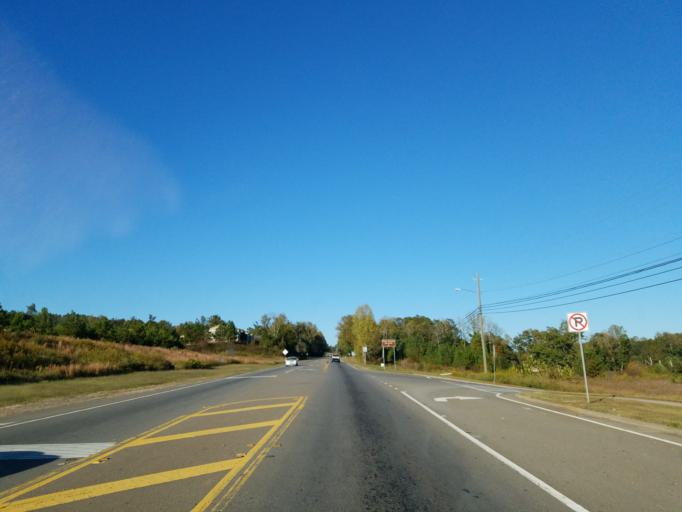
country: US
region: Georgia
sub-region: Cherokee County
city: Ball Ground
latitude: 34.3274
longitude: -84.3894
